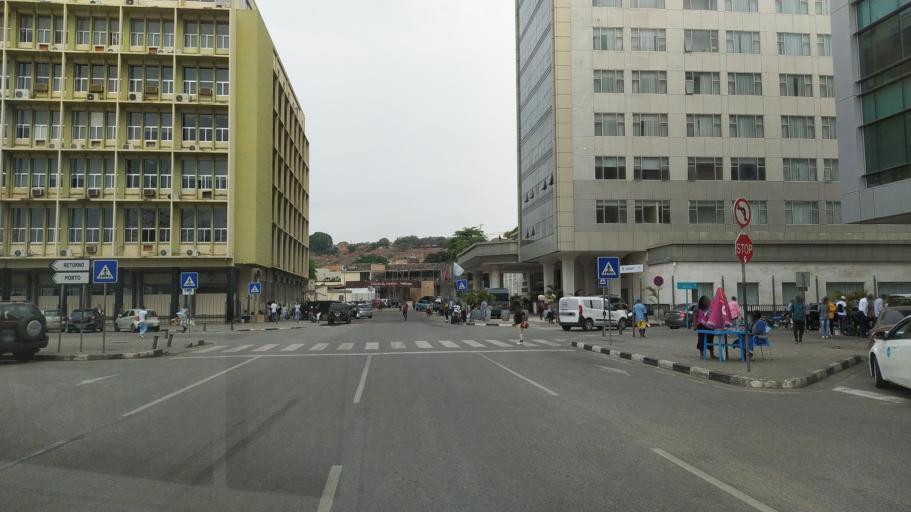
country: AO
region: Luanda
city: Luanda
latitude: -8.8034
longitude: 13.2425
